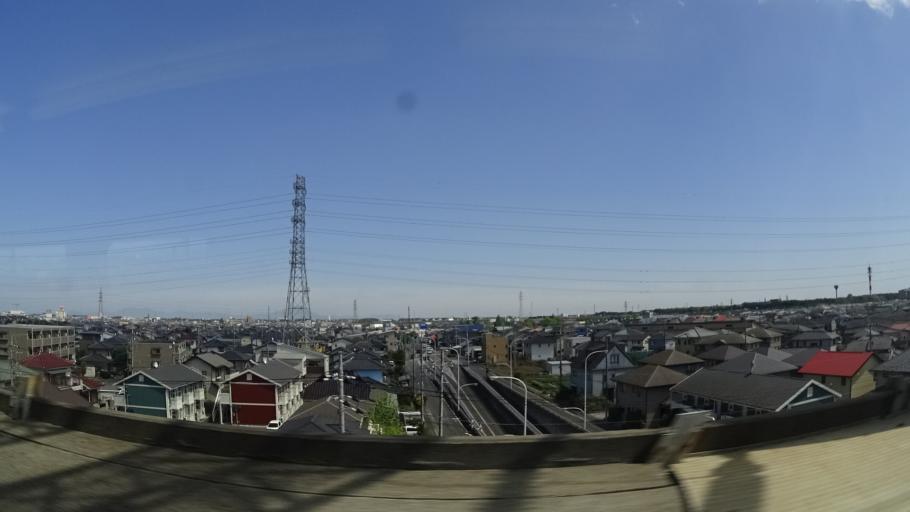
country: JP
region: Tochigi
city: Oyama
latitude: 36.2978
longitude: 139.7954
